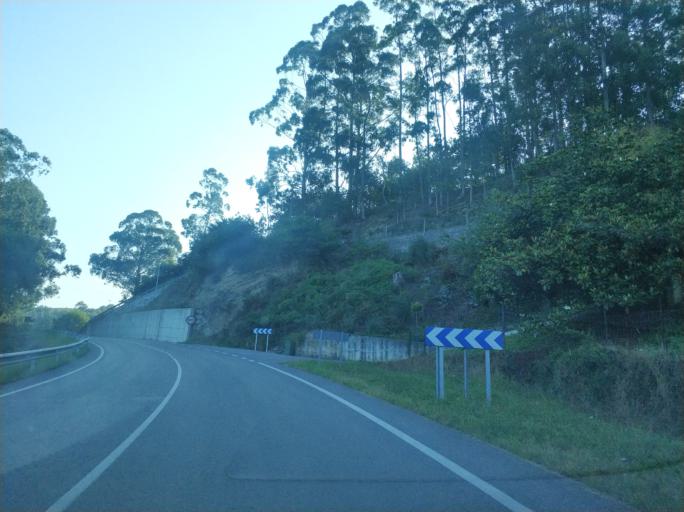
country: ES
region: Cantabria
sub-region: Provincia de Cantabria
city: Camargo
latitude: 43.3979
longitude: -3.9427
